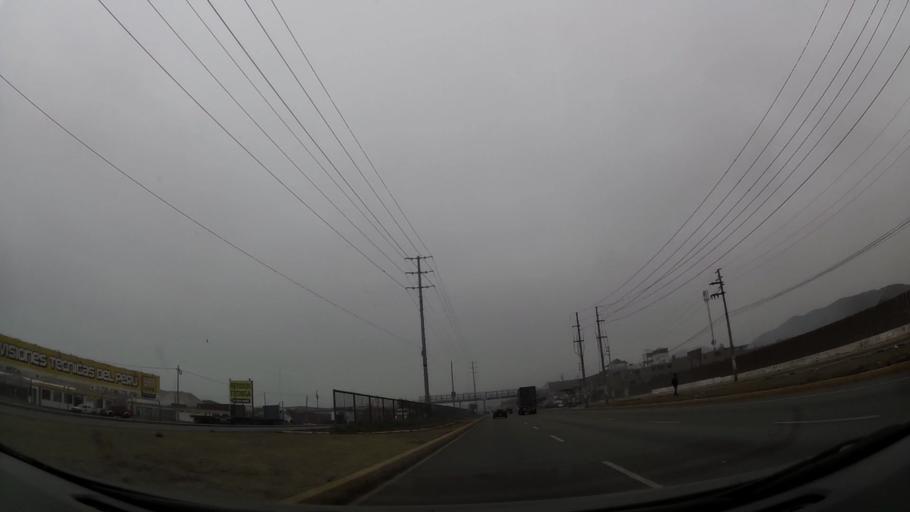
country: PE
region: Lima
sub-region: Lima
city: Independencia
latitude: -11.9739
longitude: -77.1250
